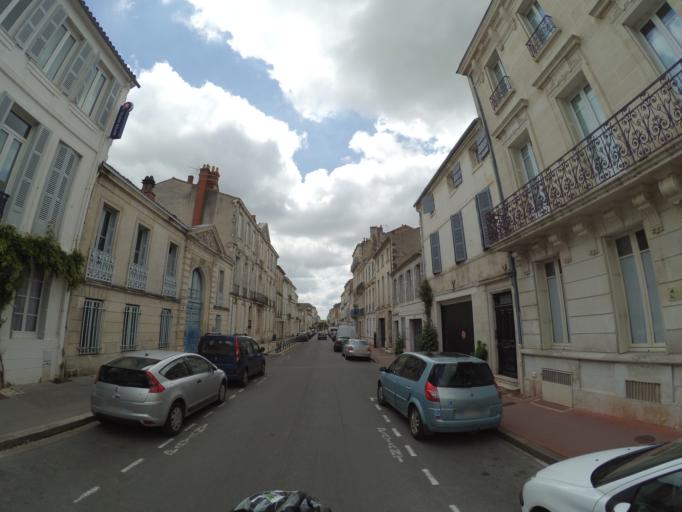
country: FR
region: Poitou-Charentes
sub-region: Departement de la Charente-Maritime
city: Rochefort
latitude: 45.9395
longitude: -0.9604
